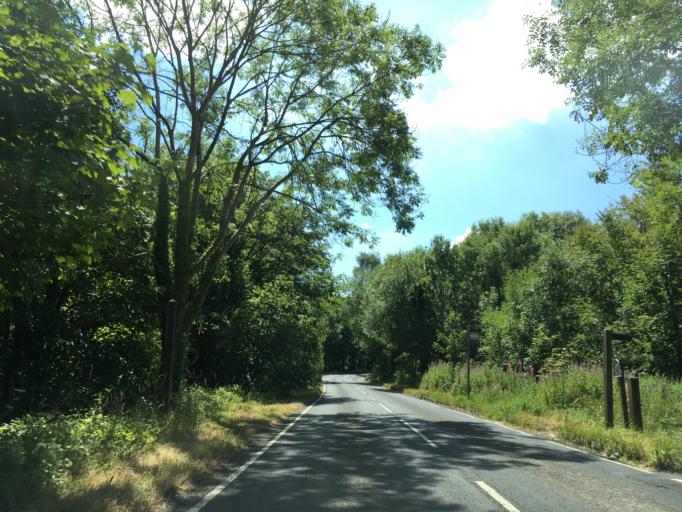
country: GB
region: England
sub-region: Gloucestershire
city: Painswick
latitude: 51.7820
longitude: -2.2258
